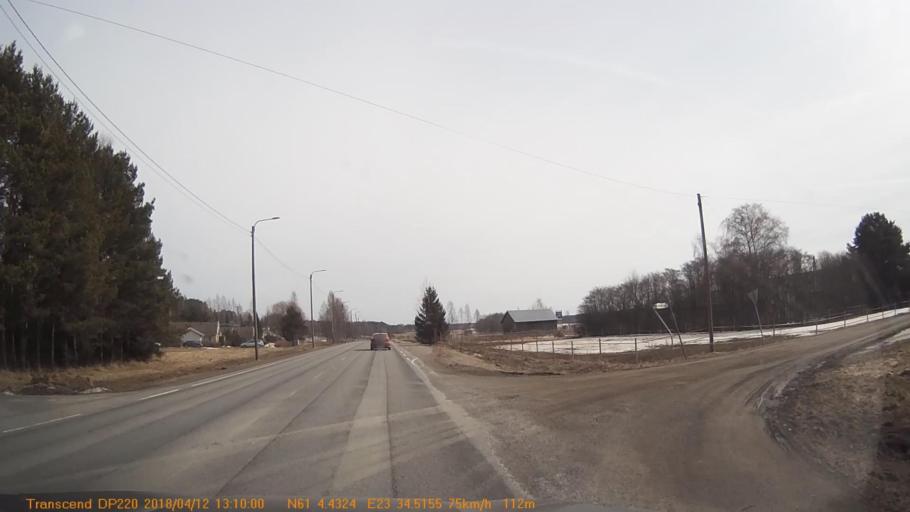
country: FI
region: Pirkanmaa
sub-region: Etelae-Pirkanmaa
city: Urjala
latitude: 61.0736
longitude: 23.5769
